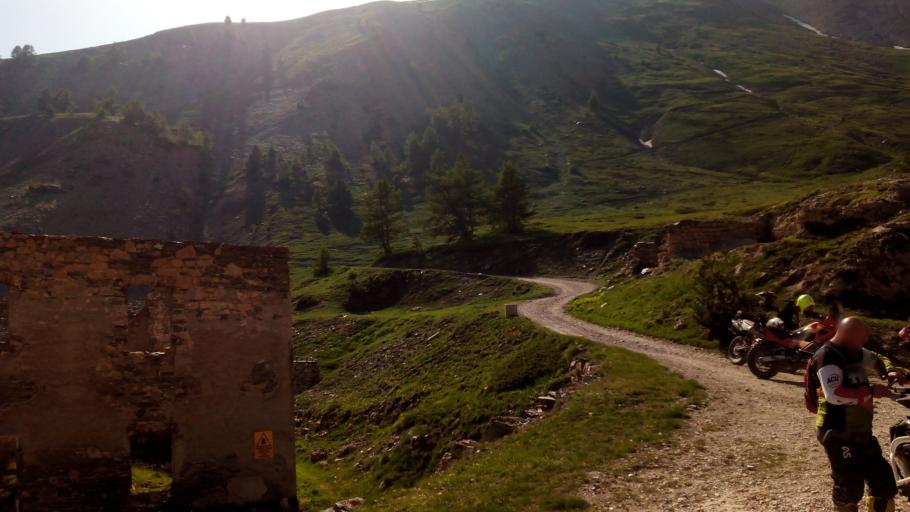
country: IT
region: Piedmont
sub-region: Provincia di Torino
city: Oulx
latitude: 45.0764
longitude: 6.8208
